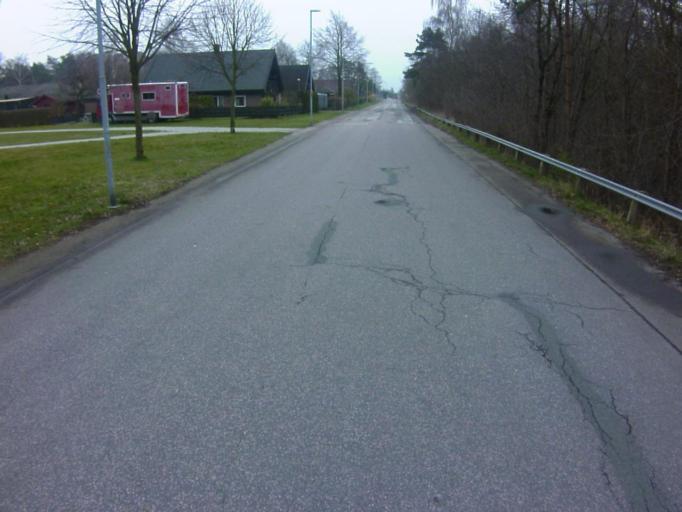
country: SE
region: Skane
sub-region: Kavlinge Kommun
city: Kaevlinge
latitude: 55.7753
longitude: 13.0800
